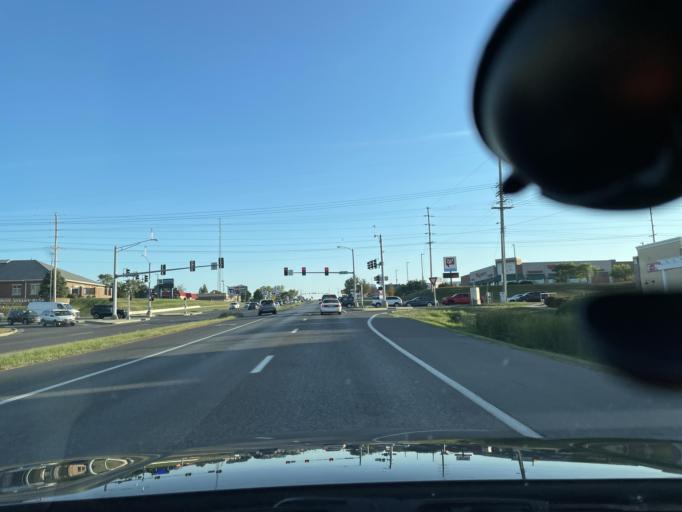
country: US
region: Missouri
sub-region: Andrew County
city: Country Club Village
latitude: 39.8073
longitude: -94.8153
